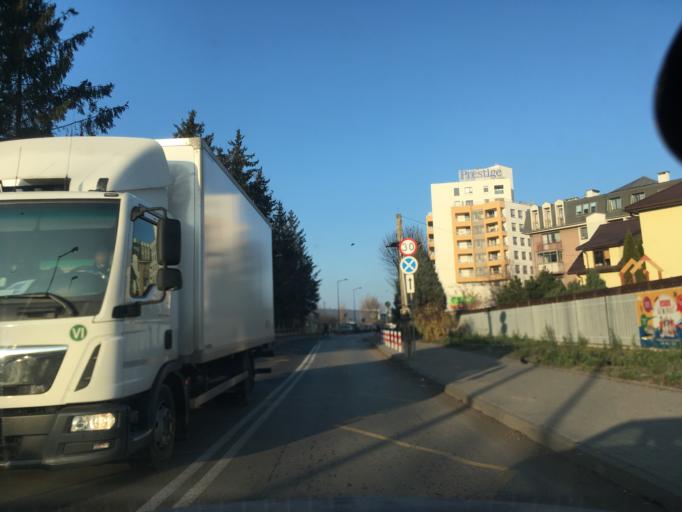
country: PL
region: Masovian Voivodeship
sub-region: Powiat piaseczynski
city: Piaseczno
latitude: 52.0762
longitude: 21.0124
